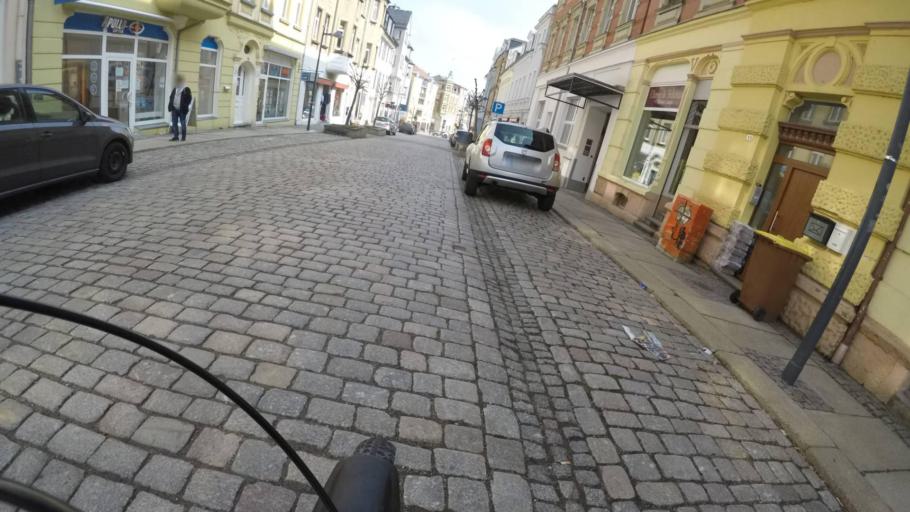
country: DE
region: Saxony
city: Limbach-Oberfrohna
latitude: 50.8587
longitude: 12.7596
